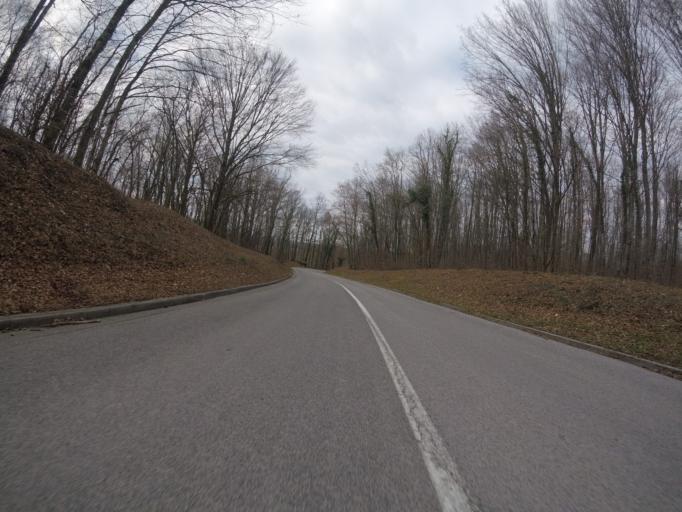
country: HR
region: Sisacko-Moslavacka
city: Glina
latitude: 45.4871
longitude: 16.0381
